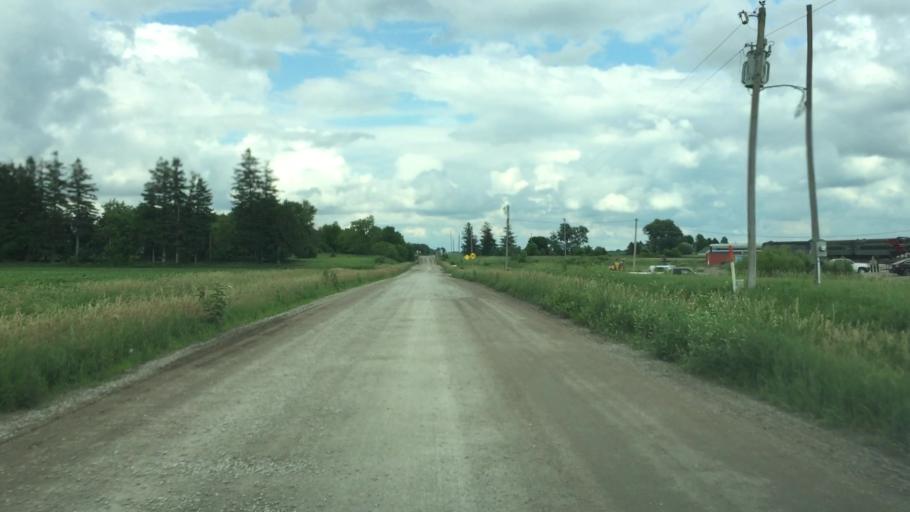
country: US
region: Iowa
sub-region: Jasper County
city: Newton
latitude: 41.7353
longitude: -93.0139
